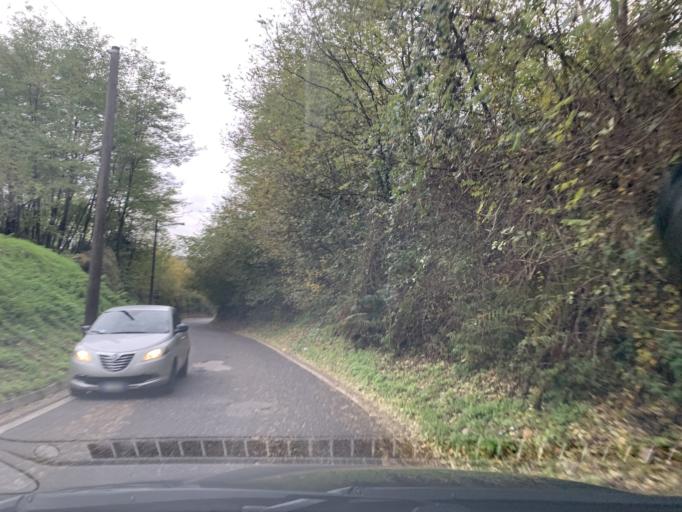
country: IT
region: Lombardy
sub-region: Provincia di Como
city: Casnate Con Bernate
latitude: 45.7464
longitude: 9.0694
